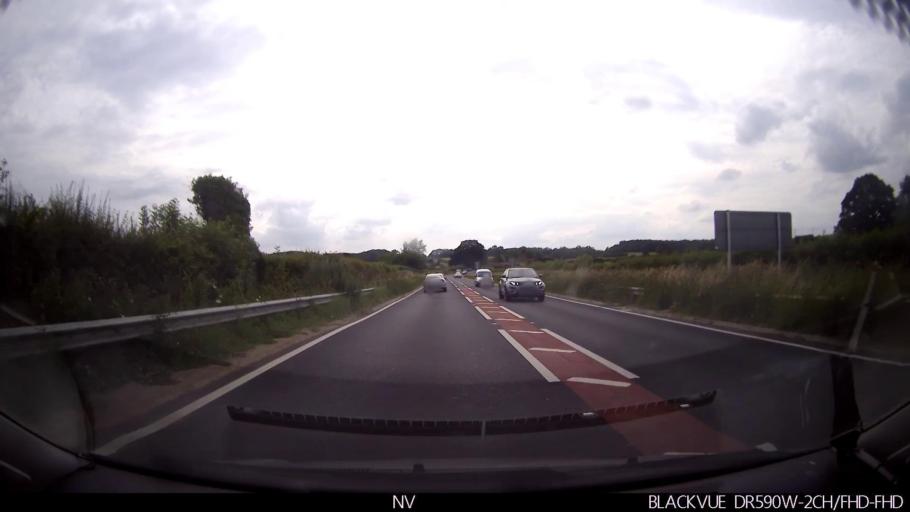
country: GB
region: England
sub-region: North Yorkshire
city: Huttons Ambo
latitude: 54.1188
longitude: -0.8303
